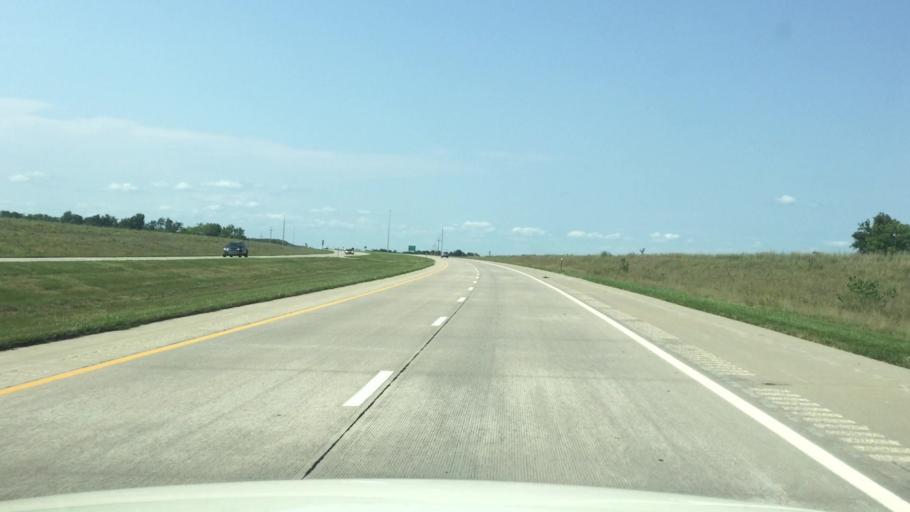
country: US
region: Kansas
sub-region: Linn County
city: Pleasanton
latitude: 38.1737
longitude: -94.6960
